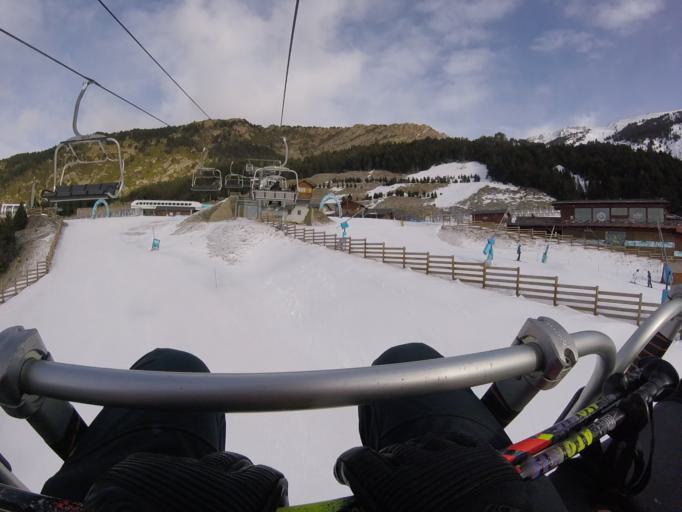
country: AD
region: Canillo
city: Canillo
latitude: 42.5551
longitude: 1.6154
